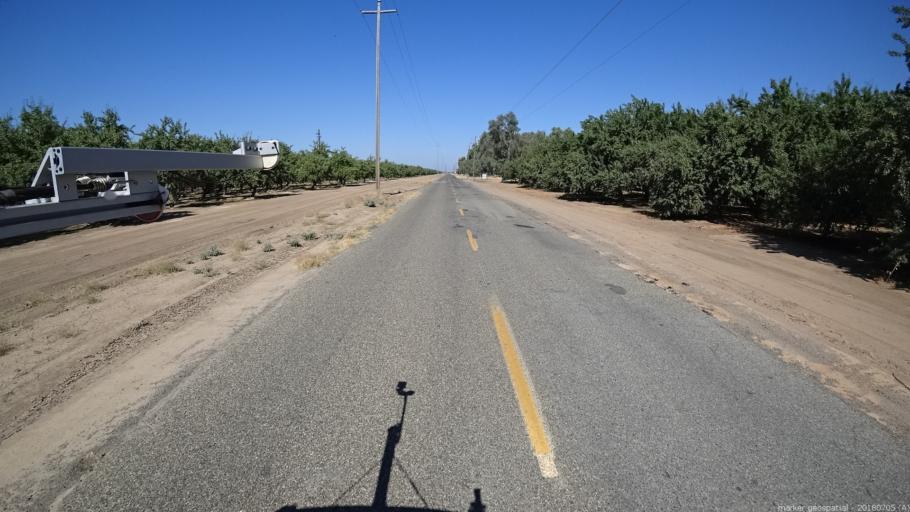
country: US
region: California
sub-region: Madera County
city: Fairmead
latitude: 37.1269
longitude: -120.1367
